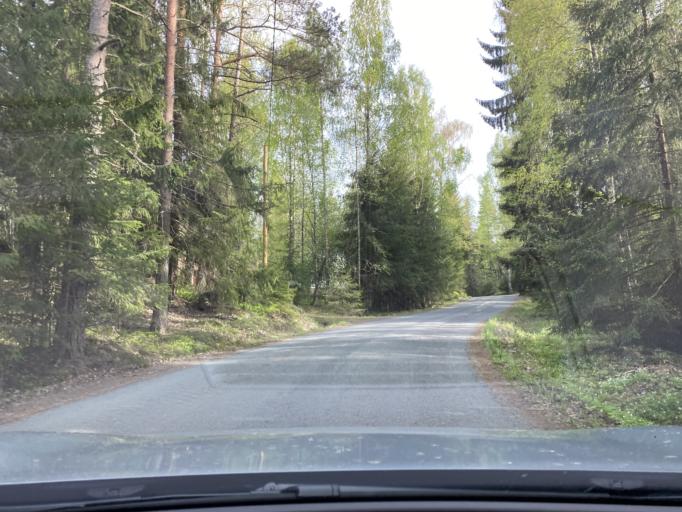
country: FI
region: Varsinais-Suomi
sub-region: Salo
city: Kiikala
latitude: 60.4523
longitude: 23.5523
